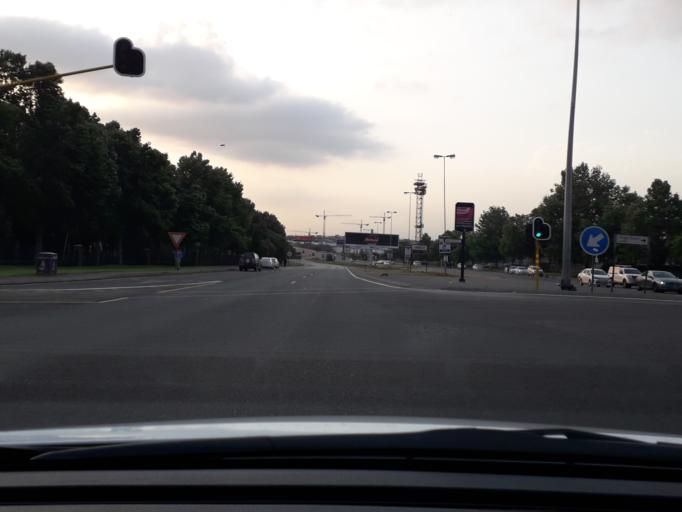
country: ZA
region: Gauteng
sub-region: City of Johannesburg Metropolitan Municipality
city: Diepsloot
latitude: -26.0235
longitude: 28.0163
